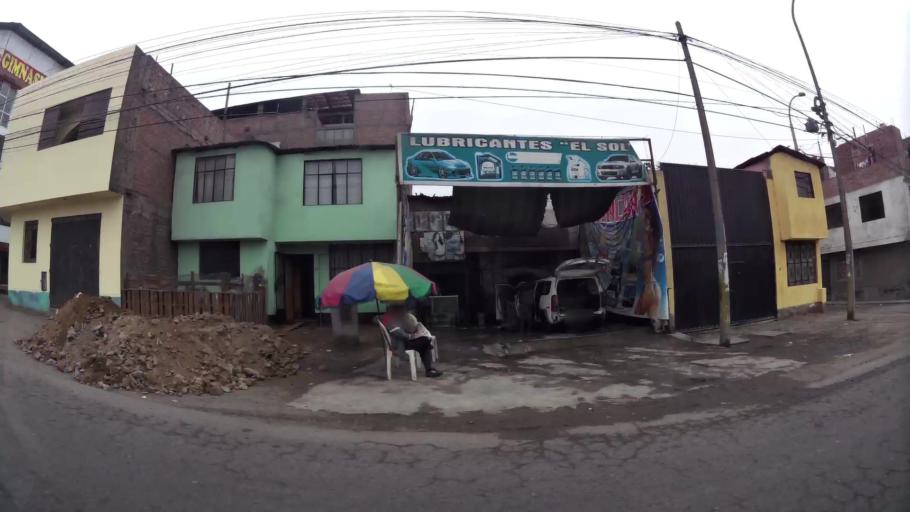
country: PE
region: Lima
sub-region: Lima
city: Independencia
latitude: -11.9494
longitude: -76.9800
